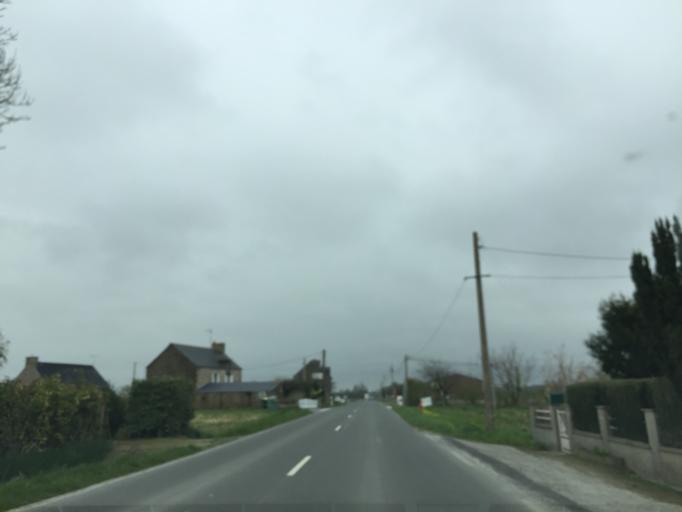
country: FR
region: Brittany
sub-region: Departement d'Ille-et-Vilaine
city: Roz-sur-Couesnon
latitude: 48.5788
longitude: -1.5624
